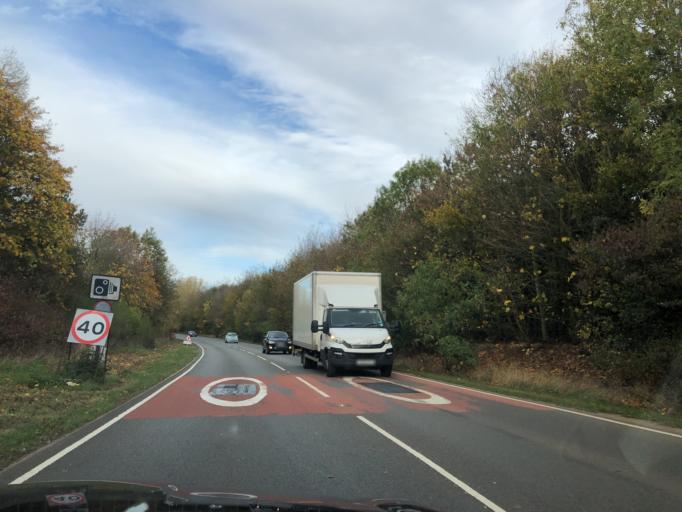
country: GB
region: England
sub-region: Warwickshire
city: Warwick
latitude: 52.2621
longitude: -1.5600
